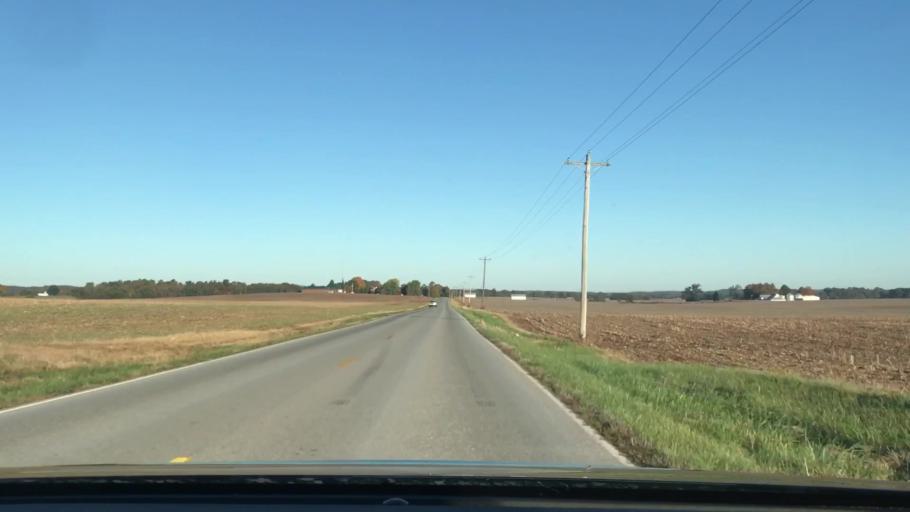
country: US
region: Kentucky
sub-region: Logan County
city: Auburn
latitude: 36.8342
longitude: -86.6868
